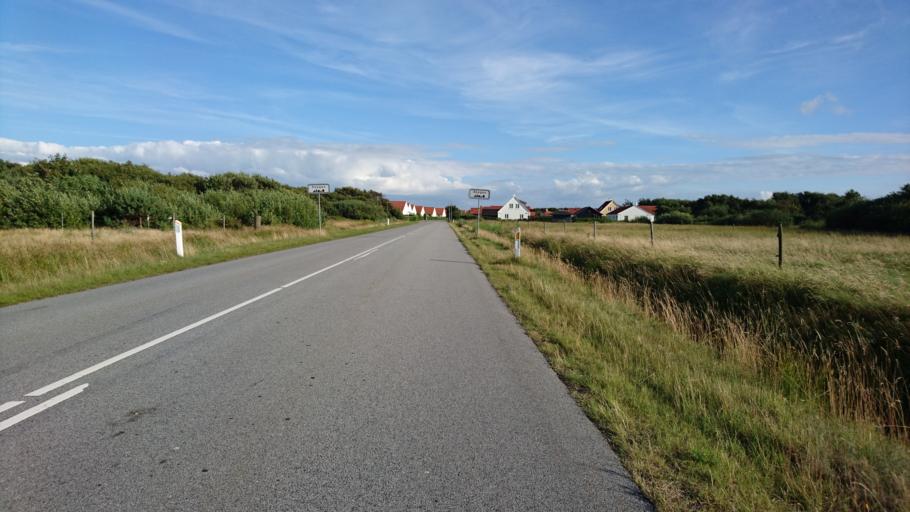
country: DK
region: North Denmark
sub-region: Frederikshavn Kommune
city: Skagen
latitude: 57.7346
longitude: 10.5810
